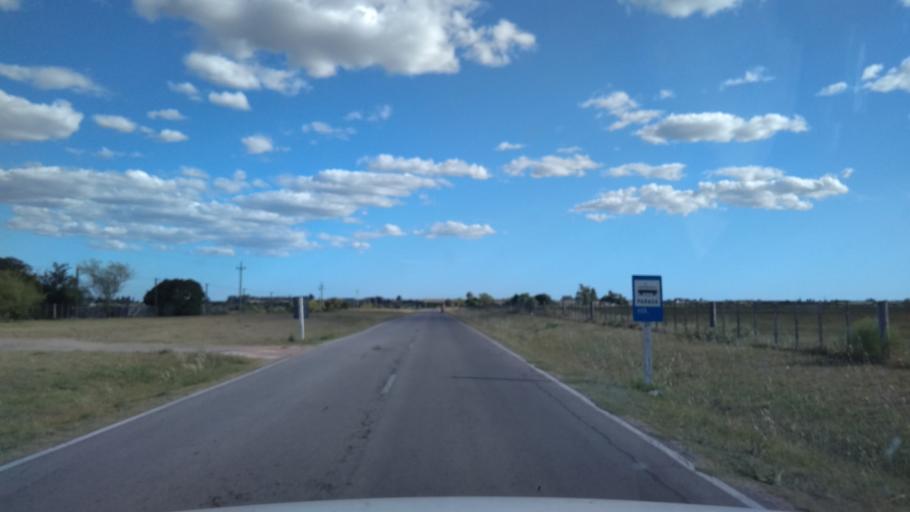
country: UY
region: Canelones
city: San Ramon
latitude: -34.3152
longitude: -55.9593
